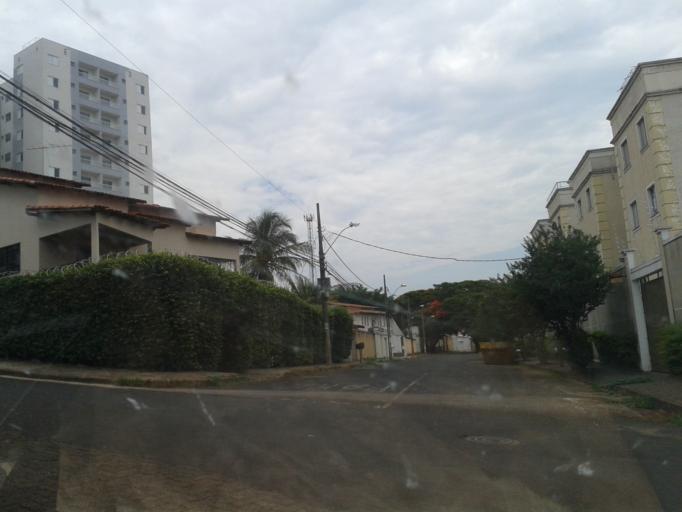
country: BR
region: Minas Gerais
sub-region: Uberlandia
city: Uberlandia
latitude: -18.9334
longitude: -48.2988
